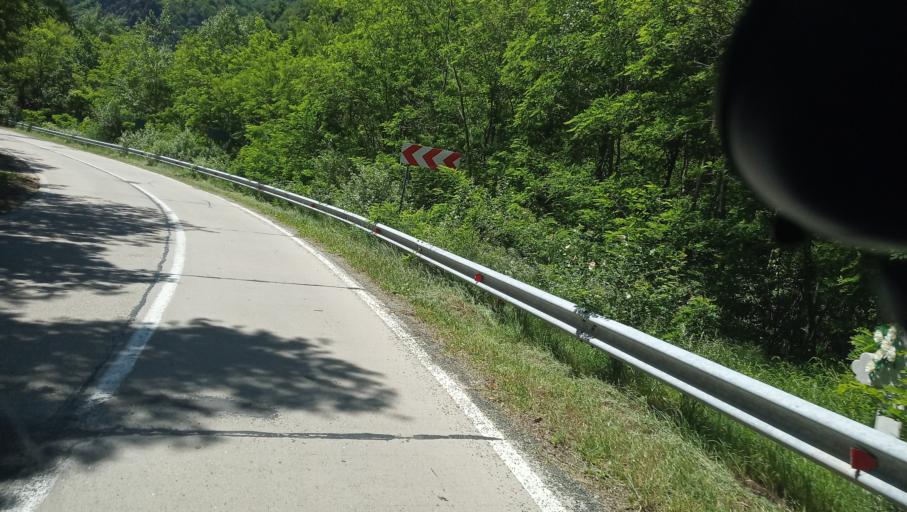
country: RO
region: Caras-Severin
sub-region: Comuna Mehadia
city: Valea Bolvasnita
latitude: 44.9519
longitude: 22.4722
